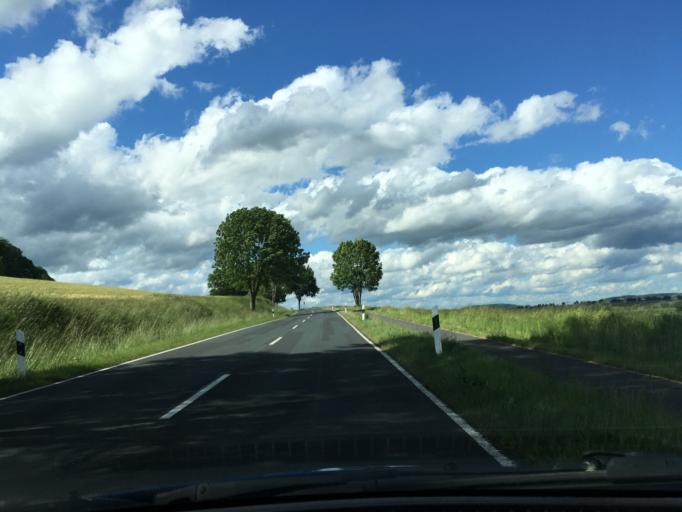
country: DE
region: Lower Saxony
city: Hardegsen
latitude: 51.6061
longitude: 9.8536
